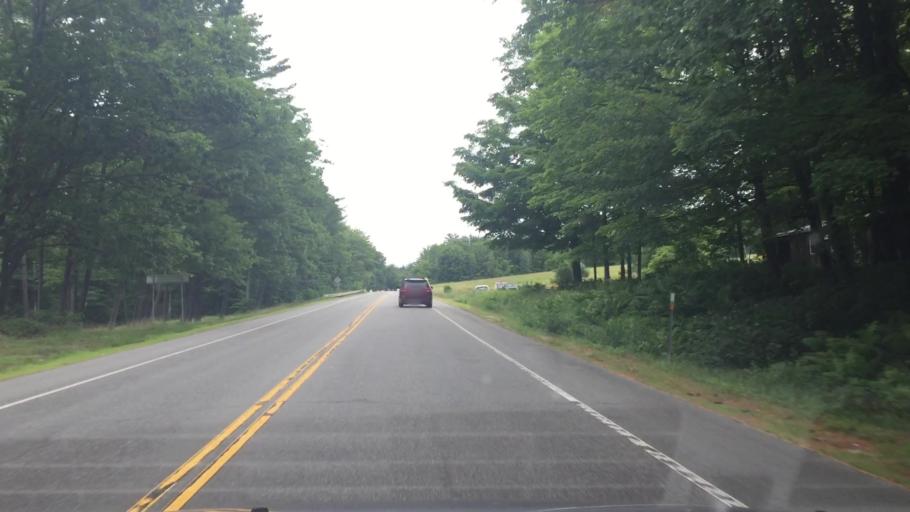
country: US
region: New Hampshire
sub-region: Grafton County
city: Ashland
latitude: 43.6230
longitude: -71.6251
